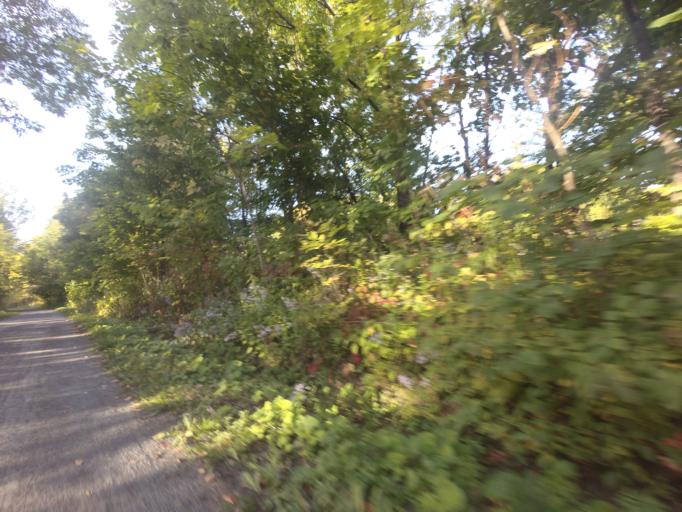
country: CA
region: Quebec
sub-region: Laurentides
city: Saint-Jerome
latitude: 45.8107
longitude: -74.0211
